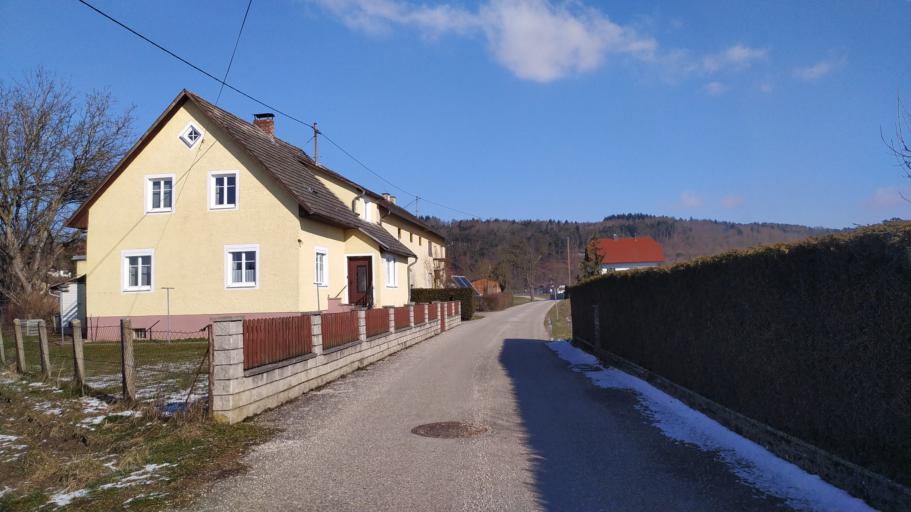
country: AT
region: Upper Austria
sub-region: Politischer Bezirk Urfahr-Umgebung
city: Feldkirchen an der Donau
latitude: 48.3595
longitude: 14.0322
